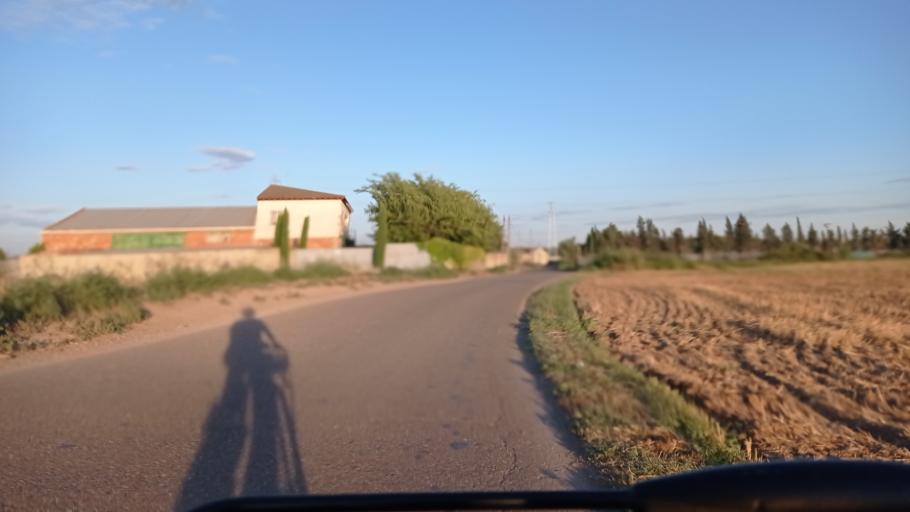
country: ES
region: Aragon
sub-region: Provincia de Zaragoza
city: Almozara
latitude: 41.6750
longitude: -0.9226
